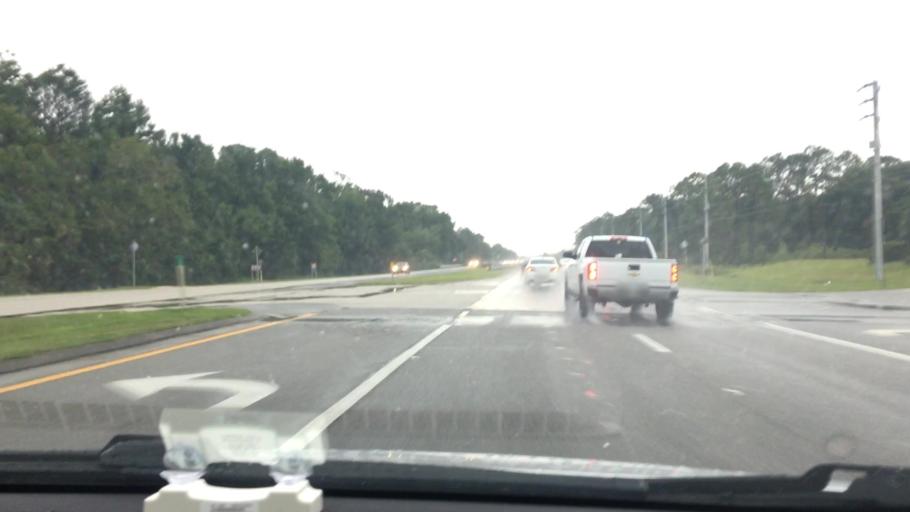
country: US
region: Florida
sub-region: Volusia County
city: Daytona Beach
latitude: 29.1651
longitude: -81.0886
